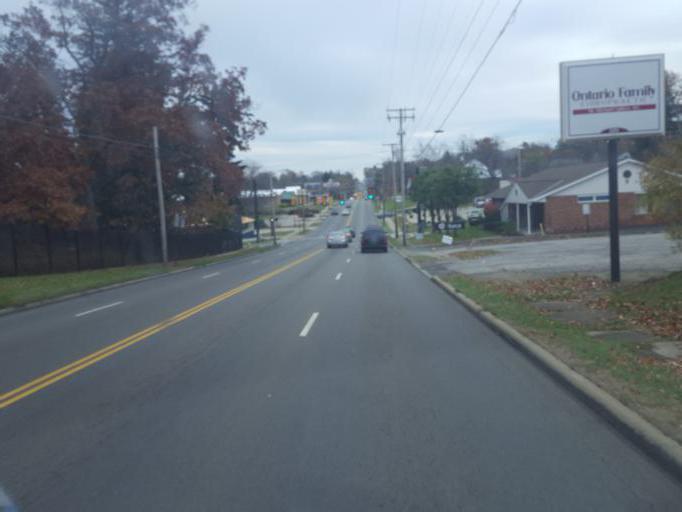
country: US
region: Ohio
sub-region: Richland County
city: Mansfield
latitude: 40.7591
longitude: -82.5483
